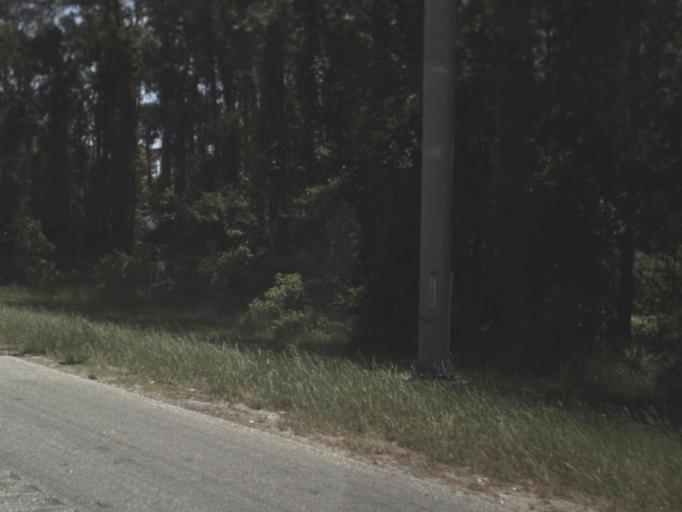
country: US
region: Florida
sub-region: Saint Johns County
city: Fruit Cove
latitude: 30.1767
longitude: -81.6214
